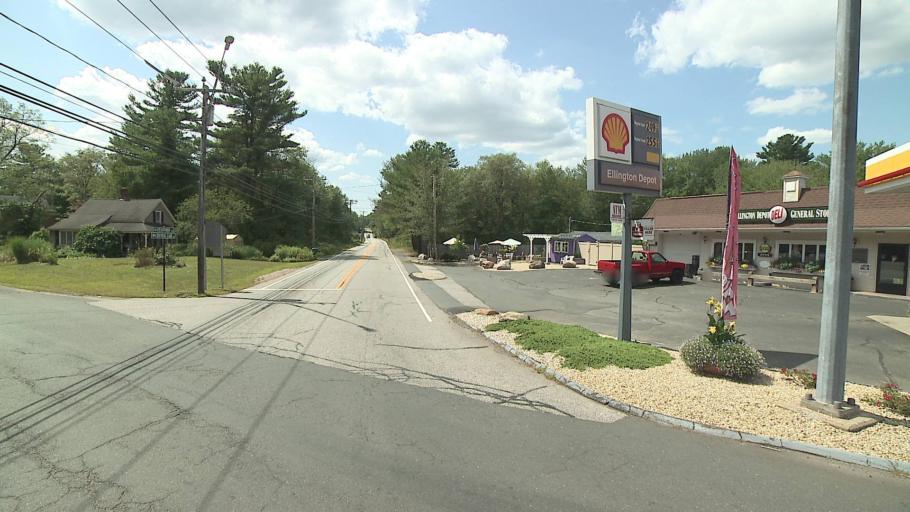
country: US
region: Connecticut
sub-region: Tolland County
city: Crystal Lake
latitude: 41.9297
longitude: -72.3831
